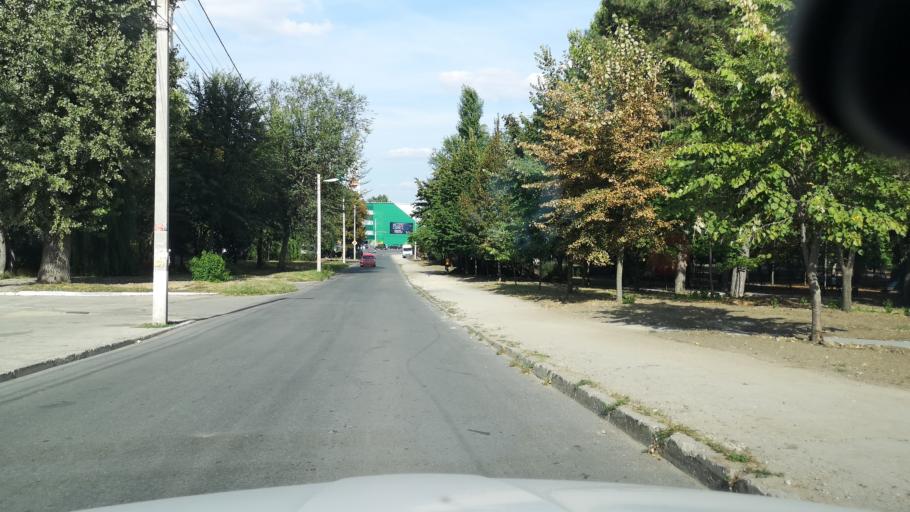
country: MD
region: Chisinau
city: Chisinau
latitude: 47.0373
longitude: 28.8022
